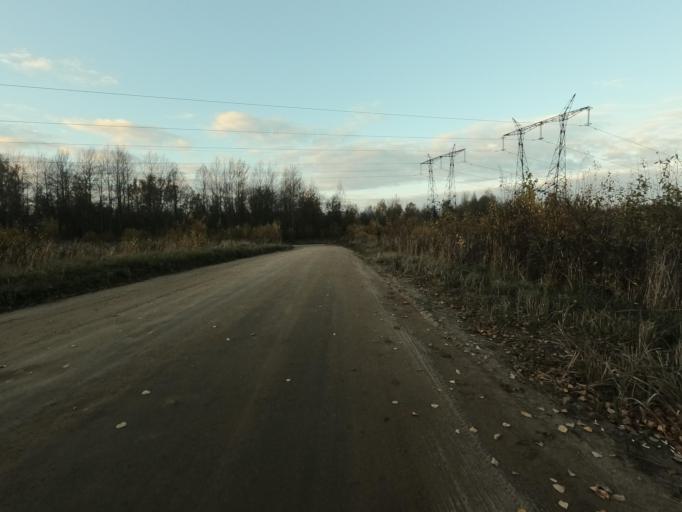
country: RU
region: Leningrad
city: Mga
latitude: 59.8060
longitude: 31.2010
